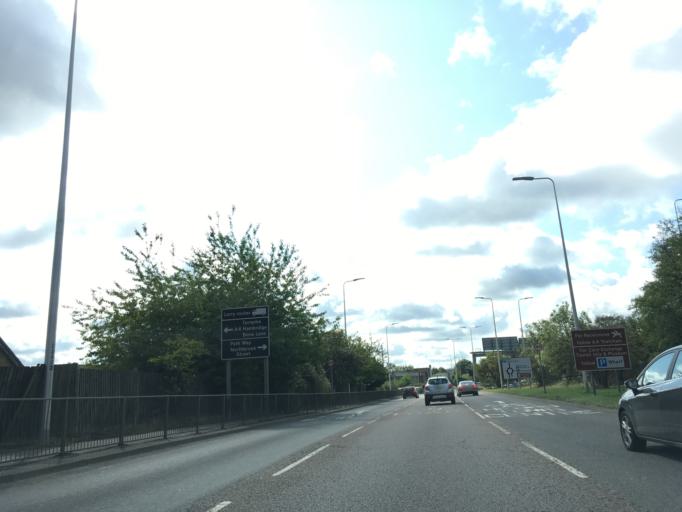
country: GB
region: England
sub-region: West Berkshire
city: Newbury
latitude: 51.4085
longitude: -1.3181
